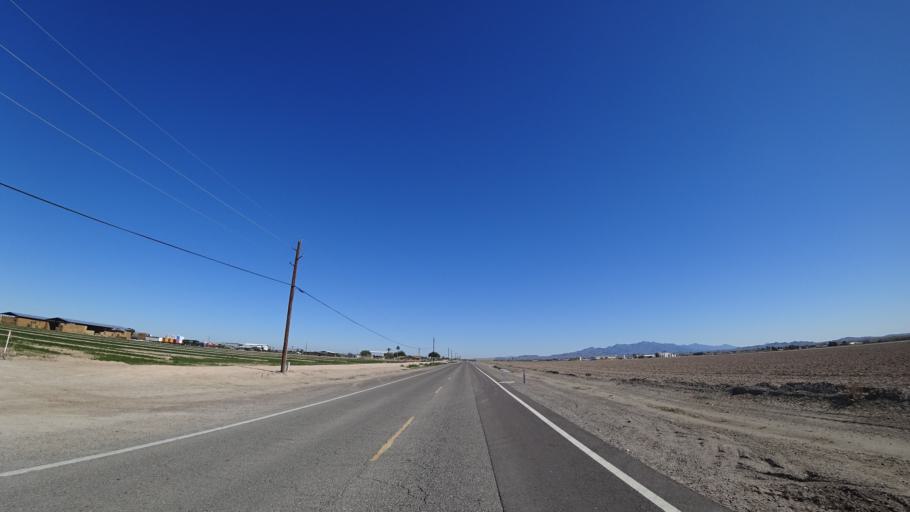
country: US
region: Arizona
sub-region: Maricopa County
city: Buckeye
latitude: 33.3924
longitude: -112.5467
